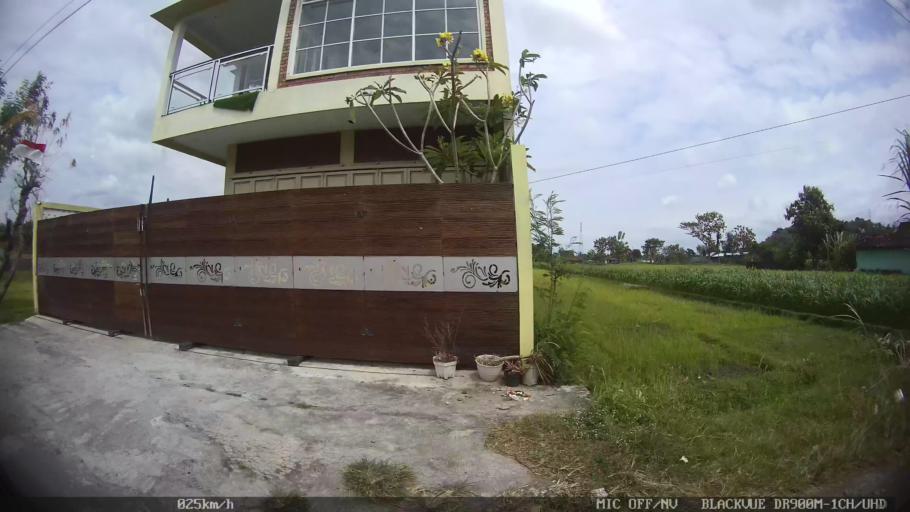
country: ID
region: Daerah Istimewa Yogyakarta
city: Depok
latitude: -7.8300
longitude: 110.4632
